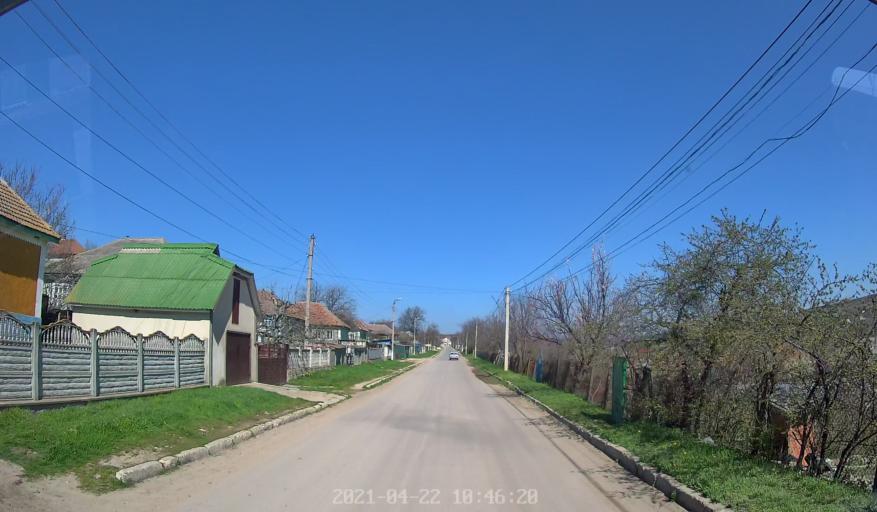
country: MD
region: Chisinau
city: Ciorescu
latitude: 47.1627
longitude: 28.9519
